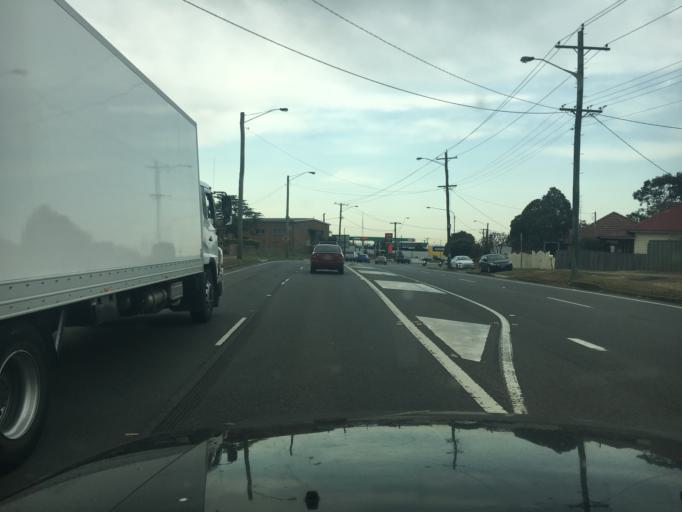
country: AU
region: New South Wales
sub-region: Maitland Municipality
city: Rutherford
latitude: -32.7190
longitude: 151.5336
